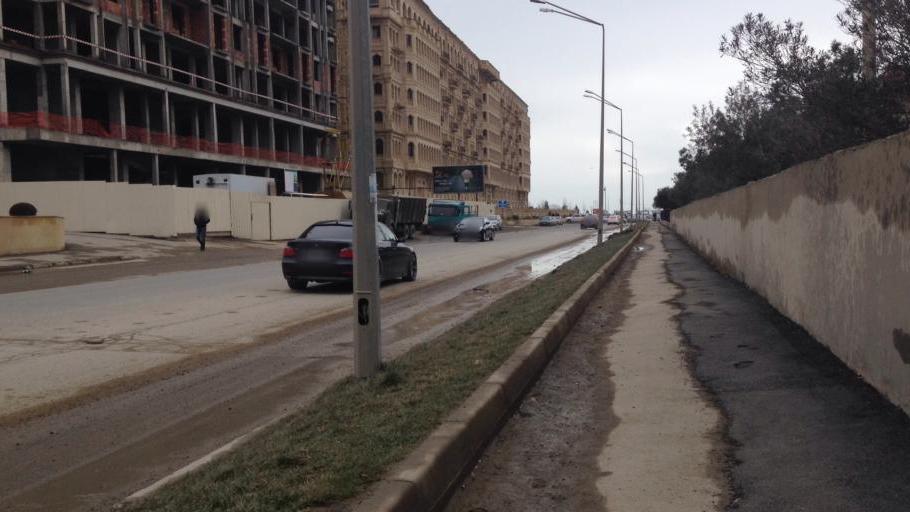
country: AZ
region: Baki
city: Baku
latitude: 40.3814
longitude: 49.8770
